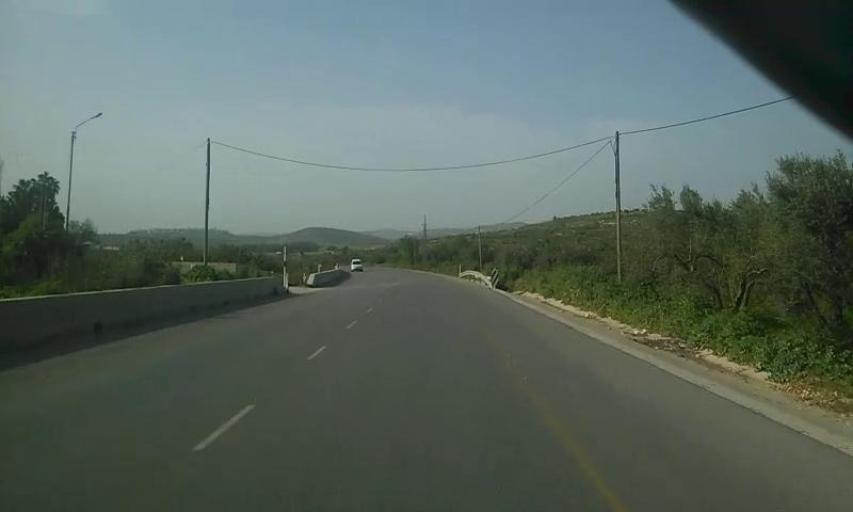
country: PS
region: West Bank
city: Dayr Sharaf
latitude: 32.2590
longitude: 35.1762
